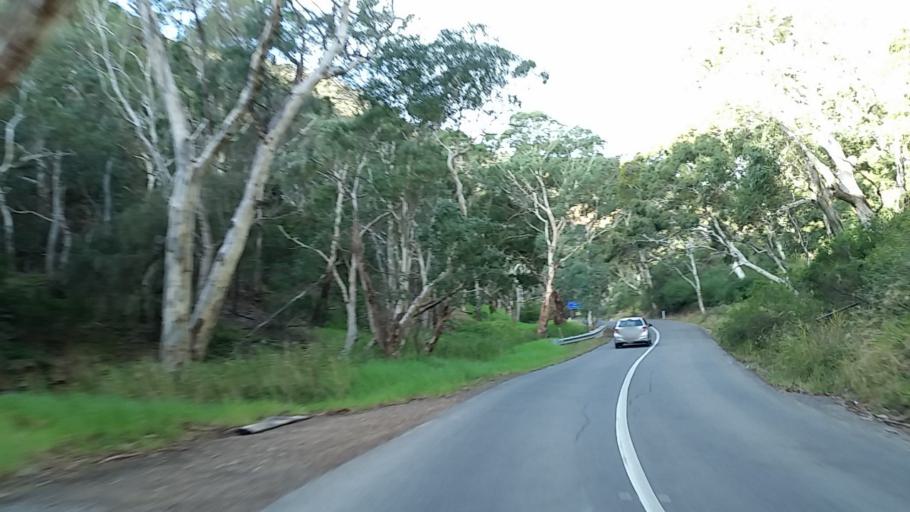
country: AU
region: South Australia
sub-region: Campbelltown
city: Athelstone
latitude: -34.8876
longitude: 138.7102
